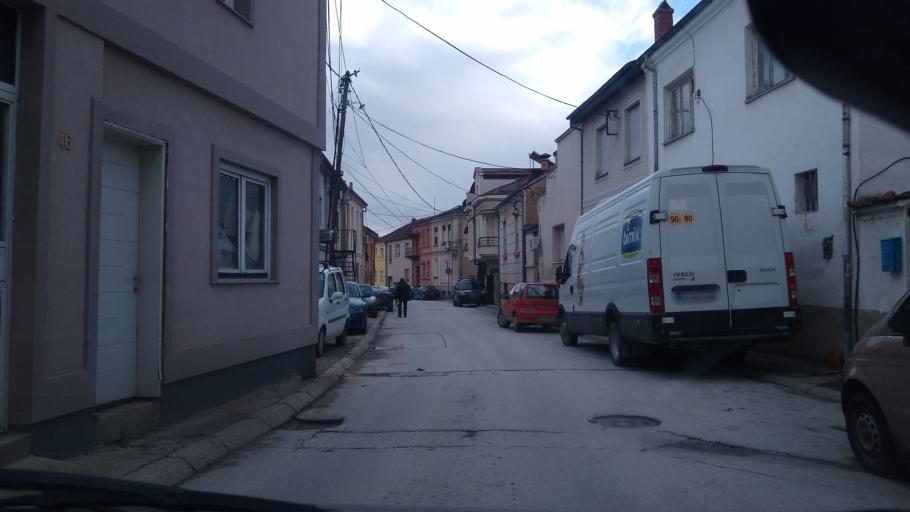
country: MK
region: Bitola
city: Bitola
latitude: 41.0257
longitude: 21.3313
